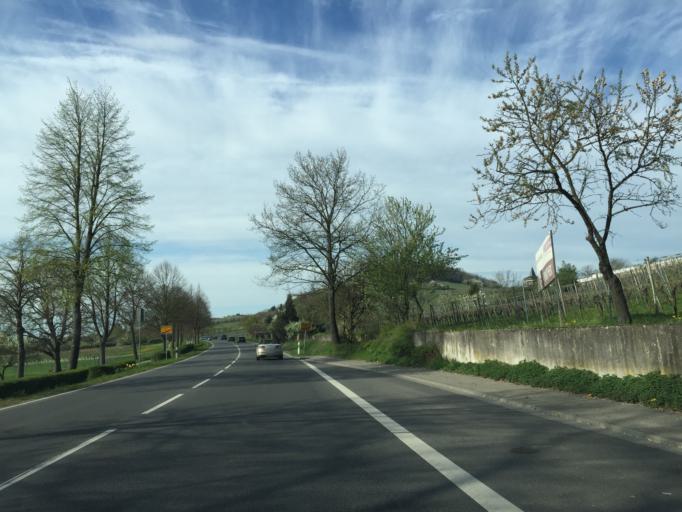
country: DE
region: Hesse
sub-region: Regierungsbezirk Darmstadt
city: Heppenheim an der Bergstrasse
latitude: 49.6557
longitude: 8.6360
